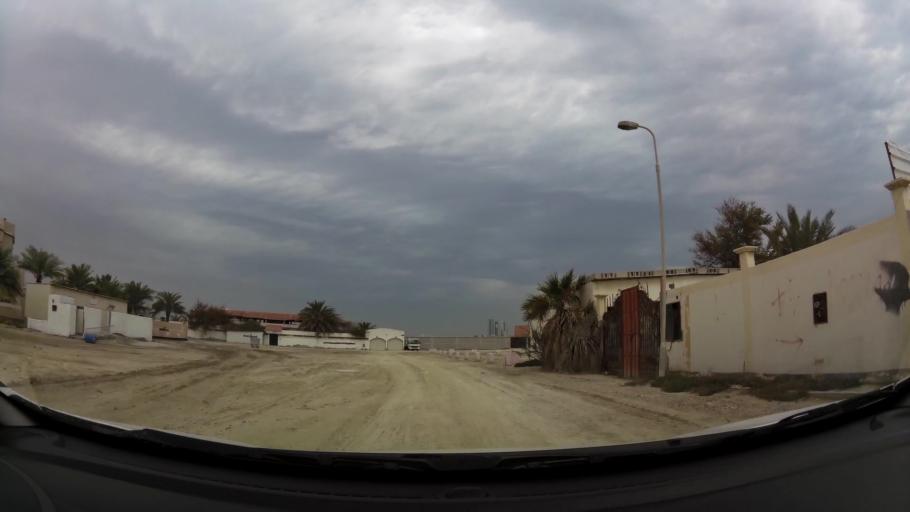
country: BH
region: Manama
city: Manama
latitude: 26.1863
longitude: 50.5833
